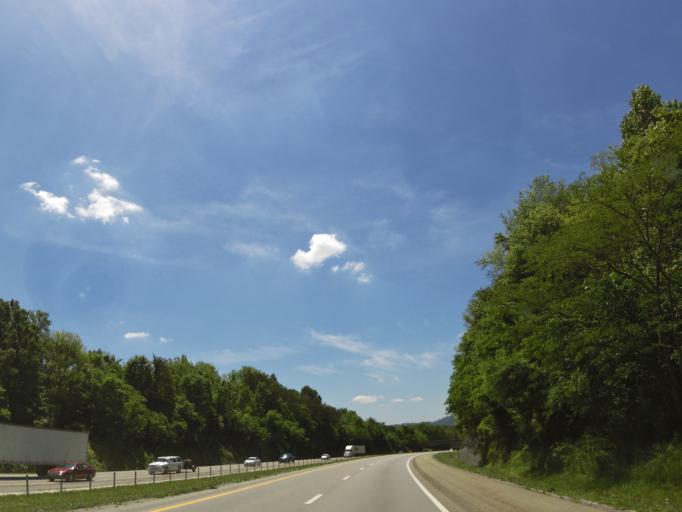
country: US
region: Kentucky
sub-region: Whitley County
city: Williamsburg
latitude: 36.6790
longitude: -84.1330
